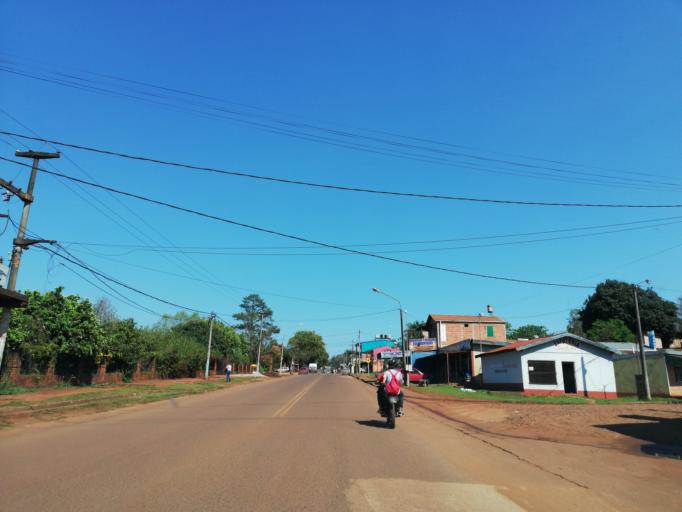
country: AR
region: Misiones
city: Puerto Eldorado
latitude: -26.4068
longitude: -54.6612
